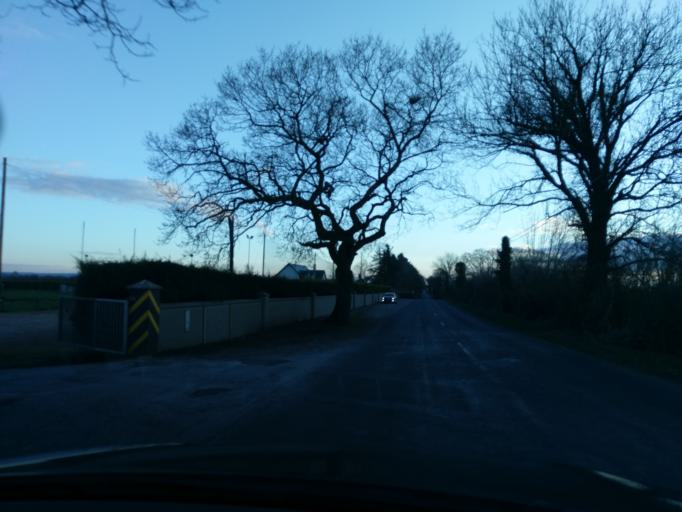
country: IE
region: Connaught
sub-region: County Galway
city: Athenry
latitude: 53.3028
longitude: -8.6242
